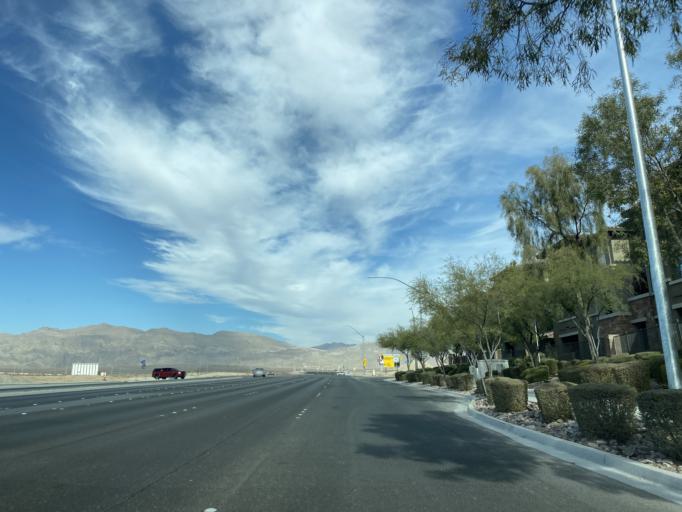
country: US
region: Nevada
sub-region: Clark County
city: Nellis Air Force Base
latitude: 36.2826
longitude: -115.1169
